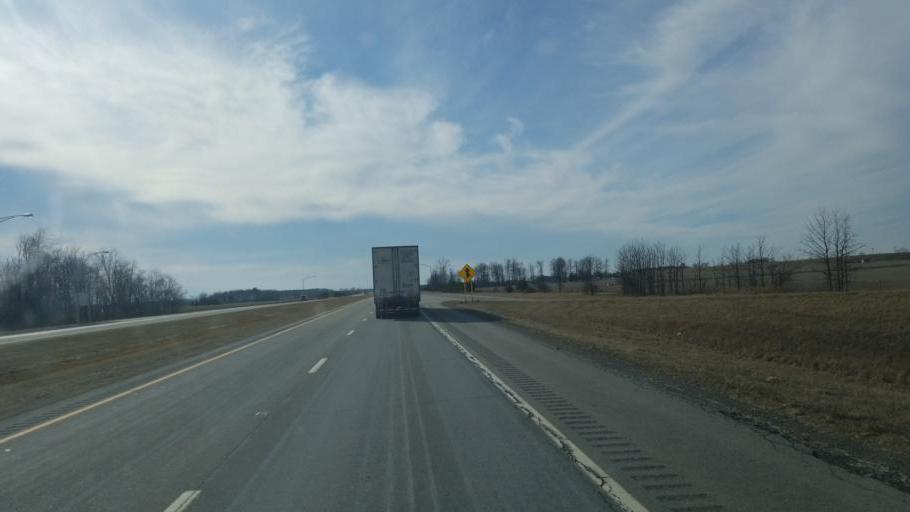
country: US
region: Ohio
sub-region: Allen County
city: Delphos
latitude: 40.8736
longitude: -84.3526
